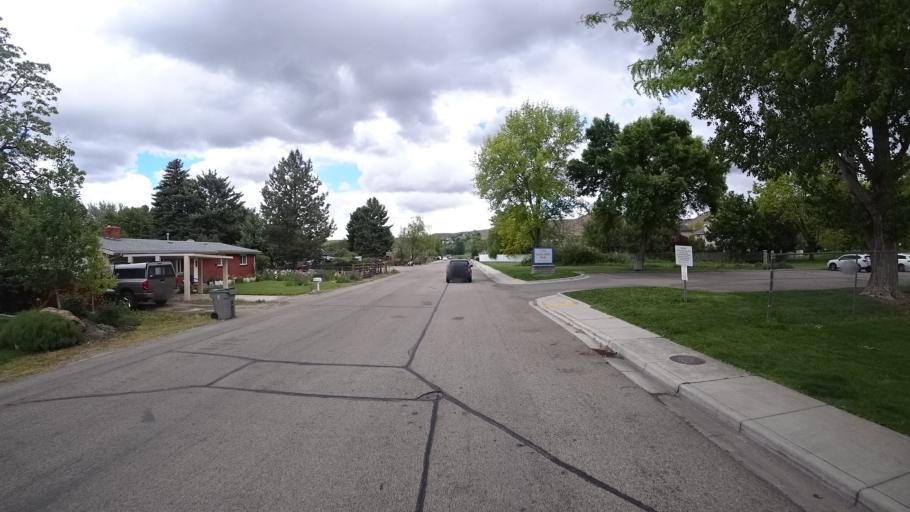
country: US
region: Idaho
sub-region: Ada County
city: Garden City
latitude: 43.6682
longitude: -116.2634
